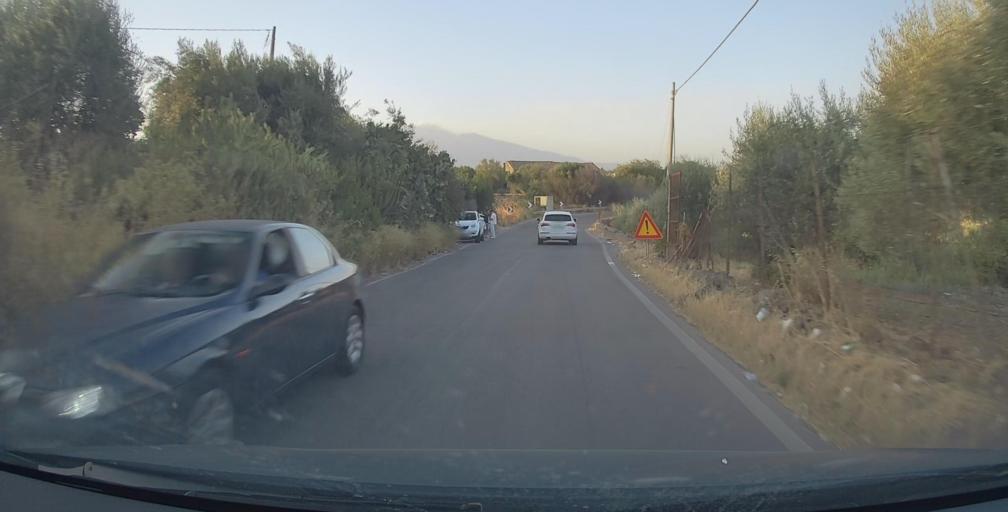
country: IT
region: Sicily
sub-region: Catania
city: Palazzolo
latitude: 37.5479
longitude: 14.9328
